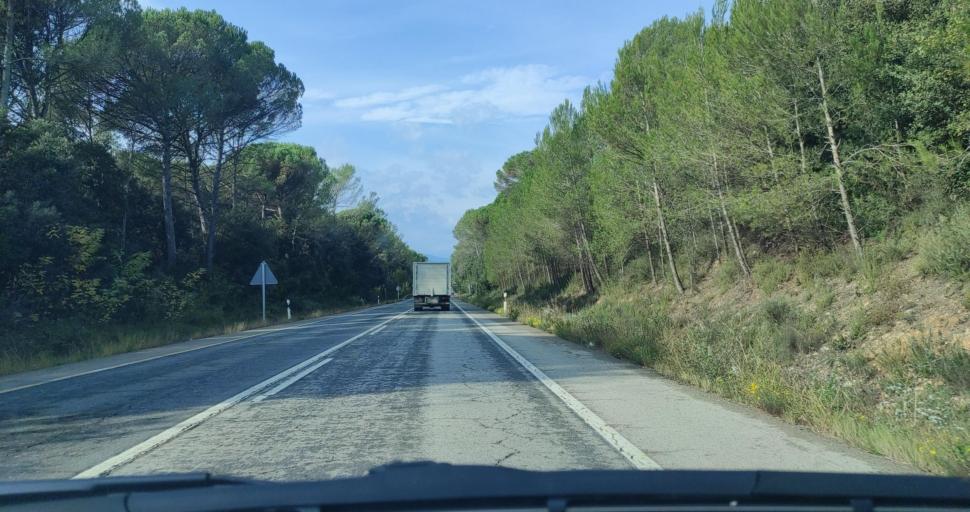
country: ES
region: Catalonia
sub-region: Provincia de Girona
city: Crespia
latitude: 42.2055
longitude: 2.7691
